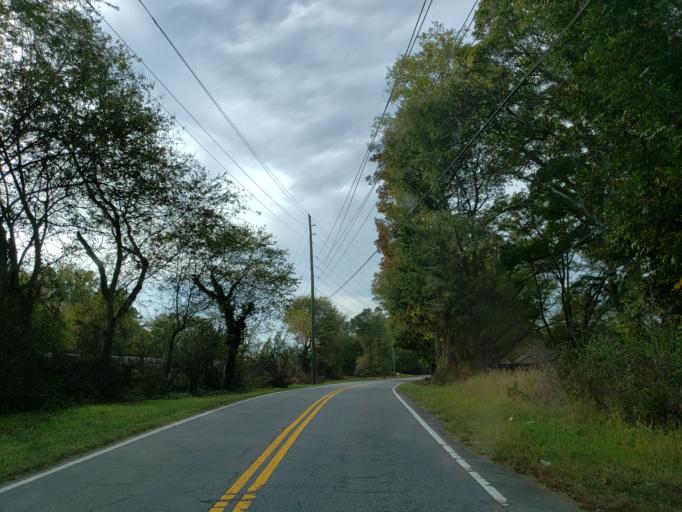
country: US
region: Georgia
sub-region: Cobb County
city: Acworth
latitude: 34.0628
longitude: -84.6520
